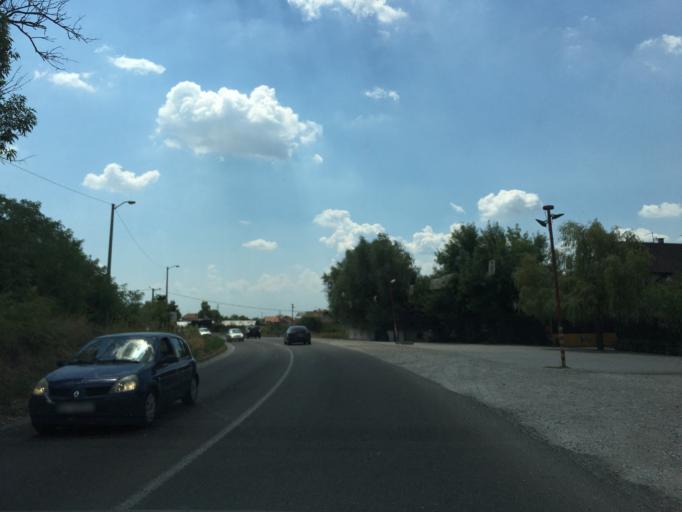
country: RS
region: Central Serbia
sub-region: Belgrade
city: Mladenovac
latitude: 44.4634
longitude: 20.6684
